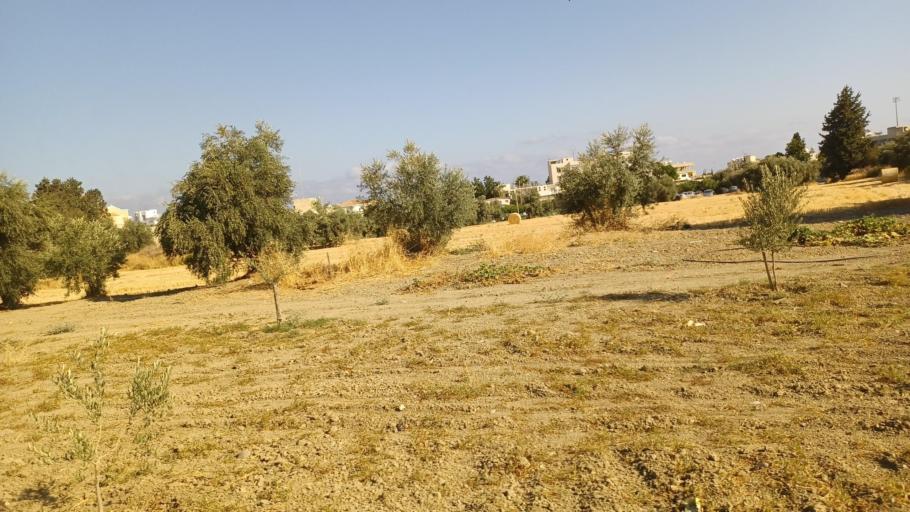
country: CY
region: Pafos
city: Polis
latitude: 35.0344
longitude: 32.4308
